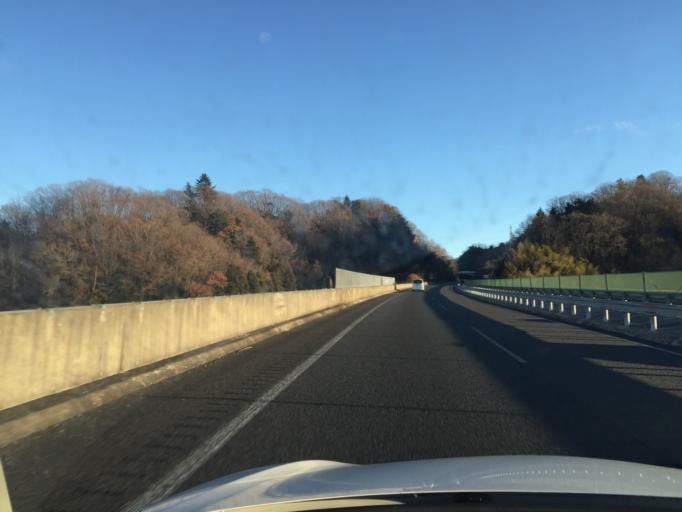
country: JP
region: Fukushima
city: Iwaki
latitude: 36.9833
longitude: 140.7979
